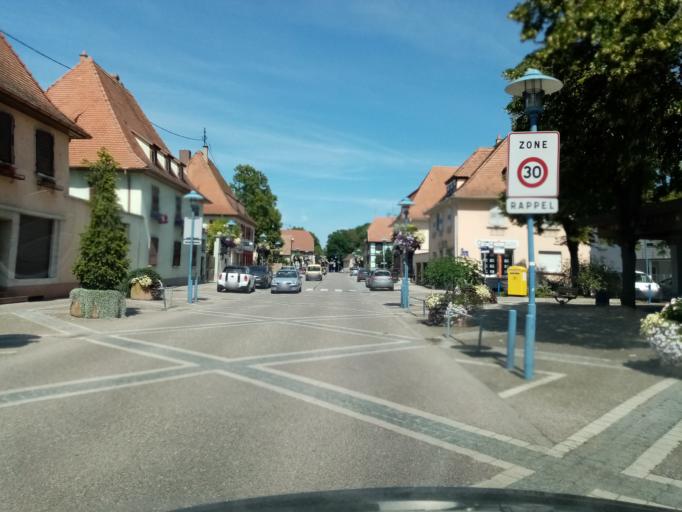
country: FR
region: Alsace
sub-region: Departement du Bas-Rhin
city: Marckolsheim
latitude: 48.1665
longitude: 7.5449
